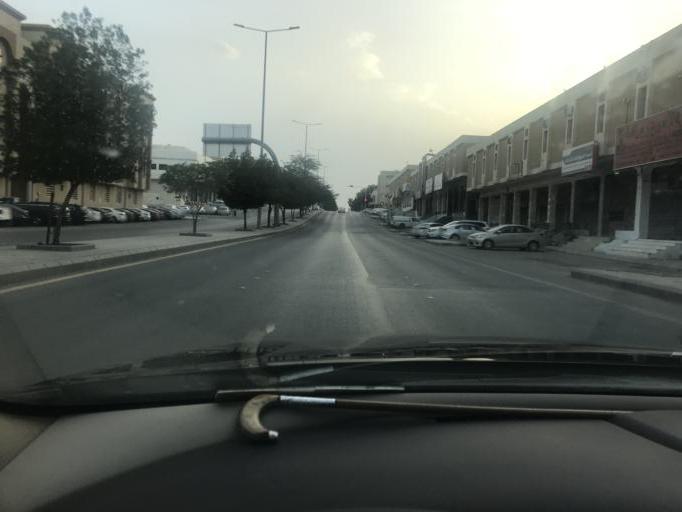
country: SA
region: Ar Riyad
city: Riyadh
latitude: 24.7283
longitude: 46.7664
